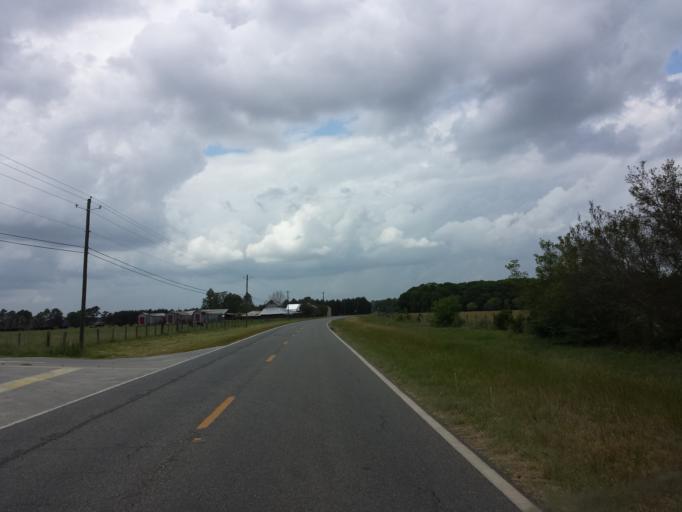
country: US
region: Georgia
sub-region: Cook County
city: Sparks
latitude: 31.1882
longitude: -83.4458
